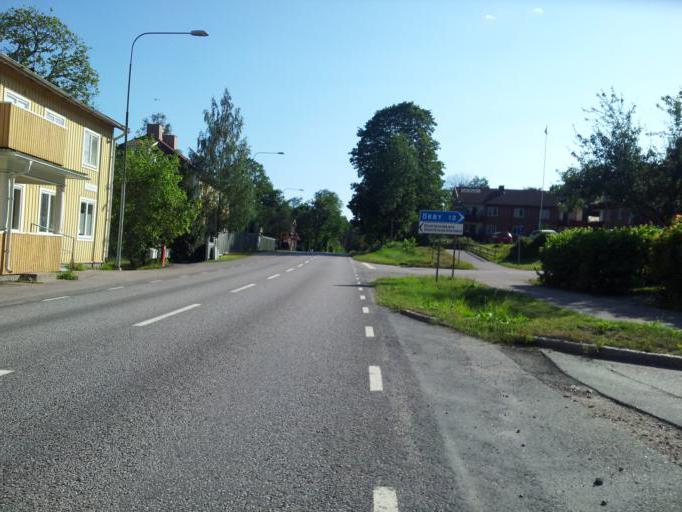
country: SE
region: Uppsala
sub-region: Knivsta Kommun
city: Knivsta
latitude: 59.8749
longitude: 17.9613
